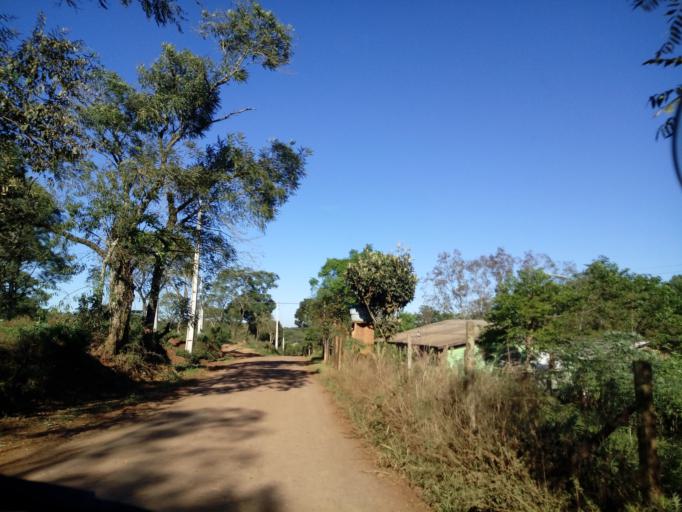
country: BR
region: Santa Catarina
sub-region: Chapeco
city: Chapeco
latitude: -27.2041
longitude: -52.6792
